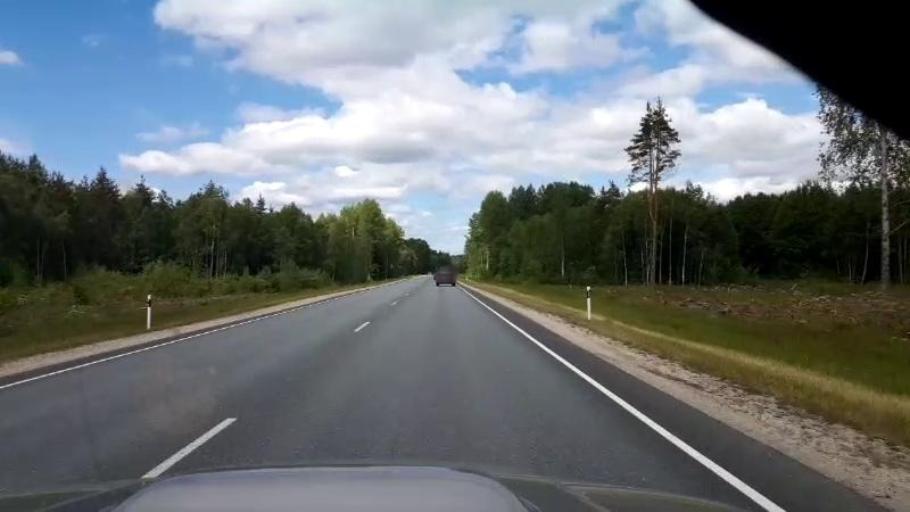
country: EE
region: Raplamaa
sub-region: Maerjamaa vald
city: Marjamaa
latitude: 59.0410
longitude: 24.4432
